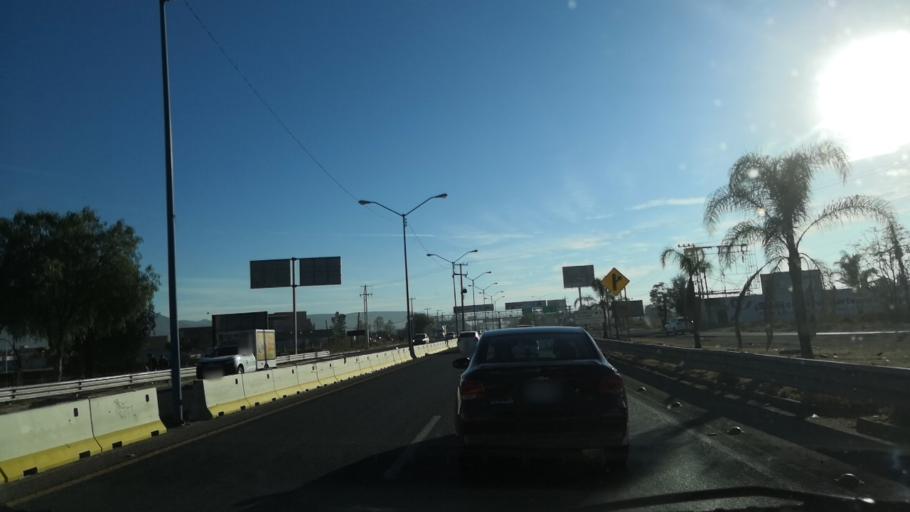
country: MX
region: Guanajuato
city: Silao
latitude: 20.9457
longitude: -101.4127
